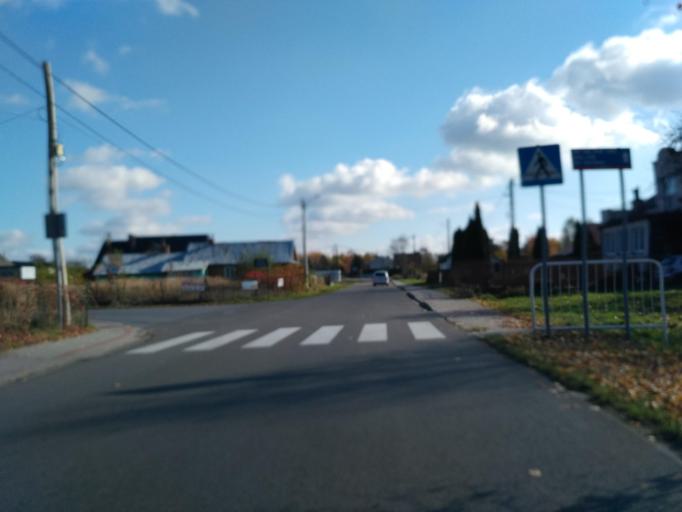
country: PL
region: Subcarpathian Voivodeship
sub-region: Powiat rzeszowski
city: Swilcza
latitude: 50.1141
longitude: 21.8731
